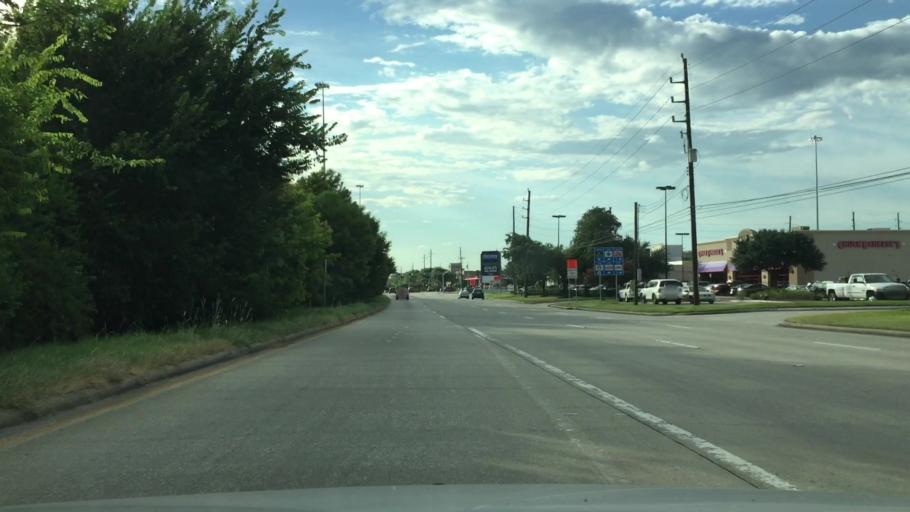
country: US
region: Texas
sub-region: Harris County
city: Hudson
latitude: 29.9592
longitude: -95.5450
